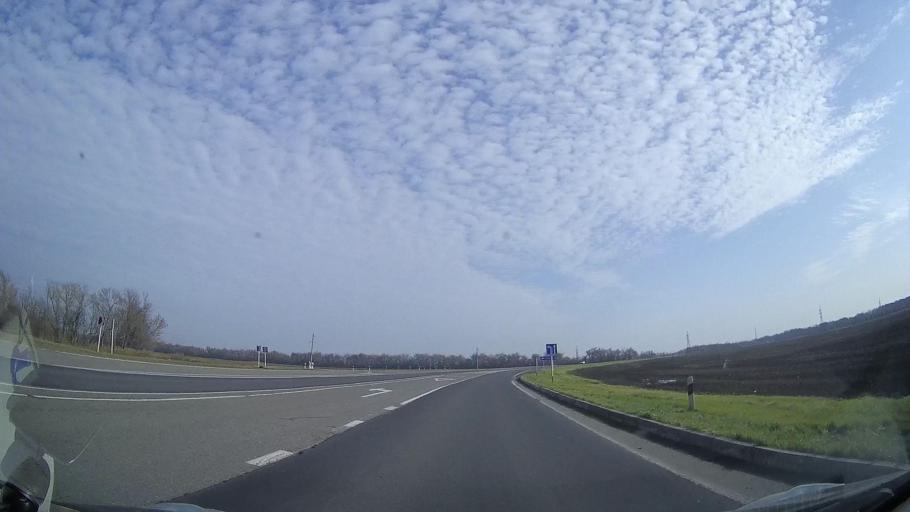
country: RU
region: Rostov
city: Tselina
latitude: 46.5325
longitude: 41.1753
